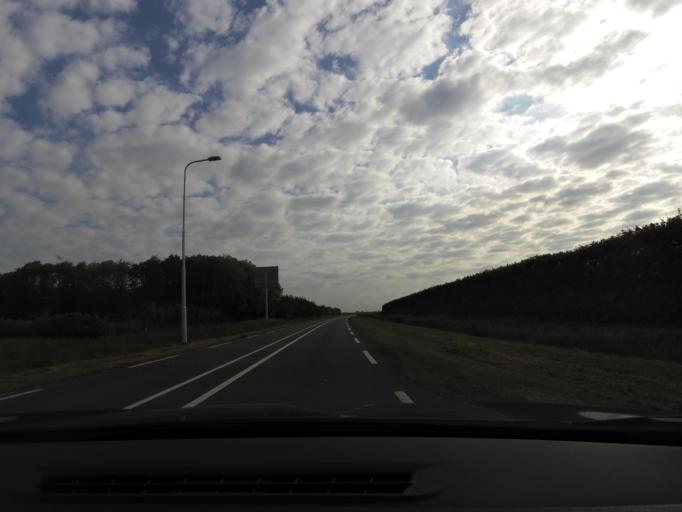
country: NL
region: Zeeland
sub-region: Schouwen-Duiveland
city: Haamstede
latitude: 51.7005
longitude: 3.7490
